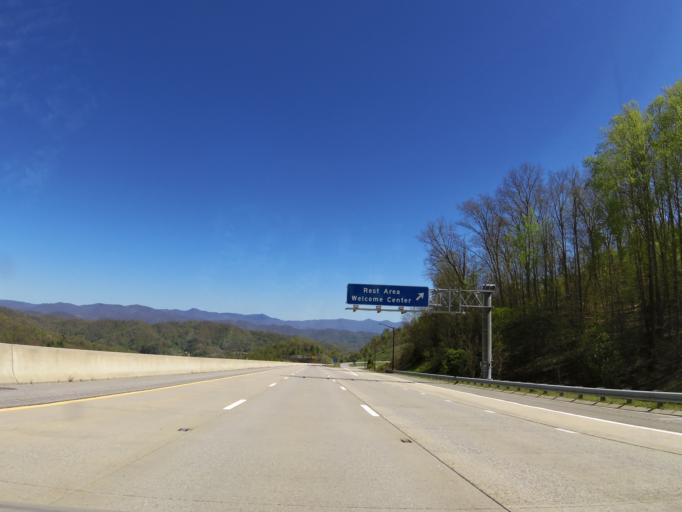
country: US
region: North Carolina
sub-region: Madison County
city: Mars Hill
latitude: 35.8773
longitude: -82.5467
